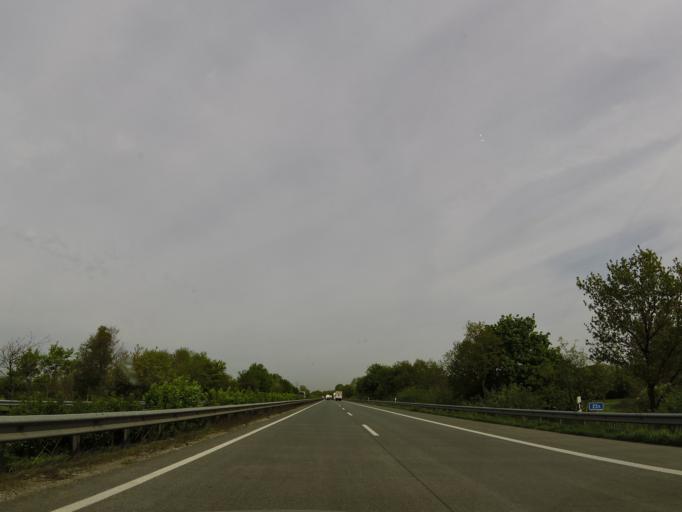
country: DE
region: Schleswig-Holstein
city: Kolln-Reisiek
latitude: 53.7674
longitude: 9.7075
